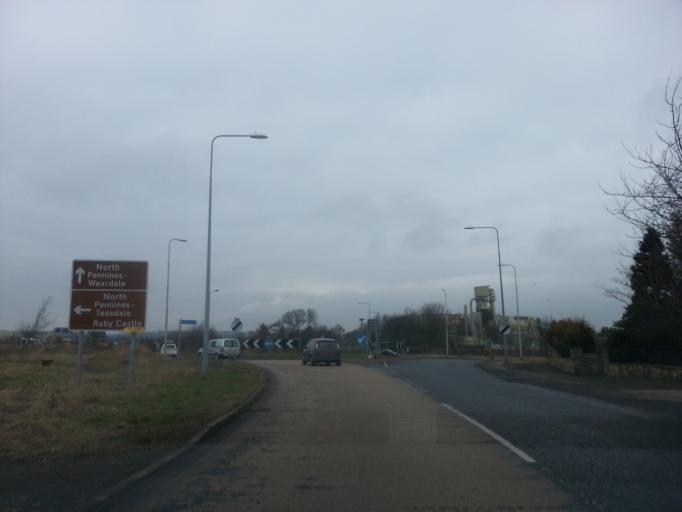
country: GB
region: England
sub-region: County Durham
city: High Etherley
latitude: 54.6254
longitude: -1.7110
